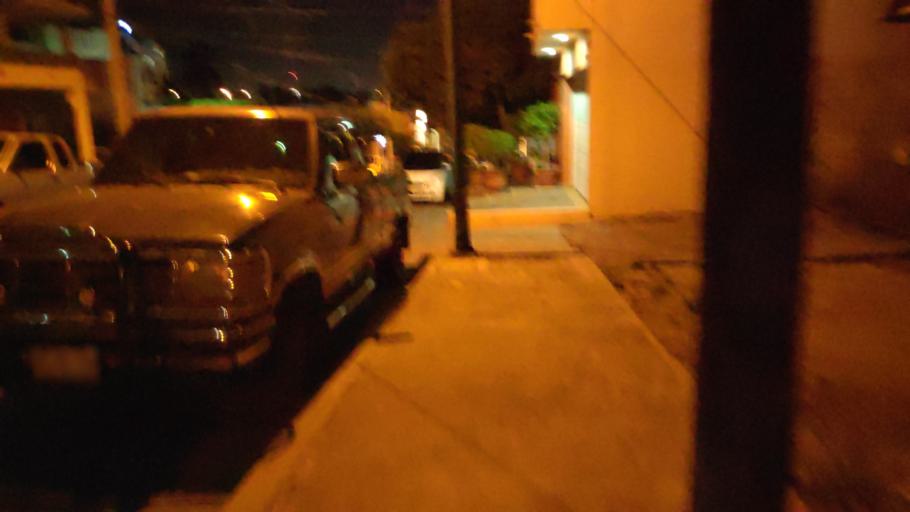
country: MX
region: Sinaloa
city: Culiacan
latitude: 24.7923
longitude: -107.4083
